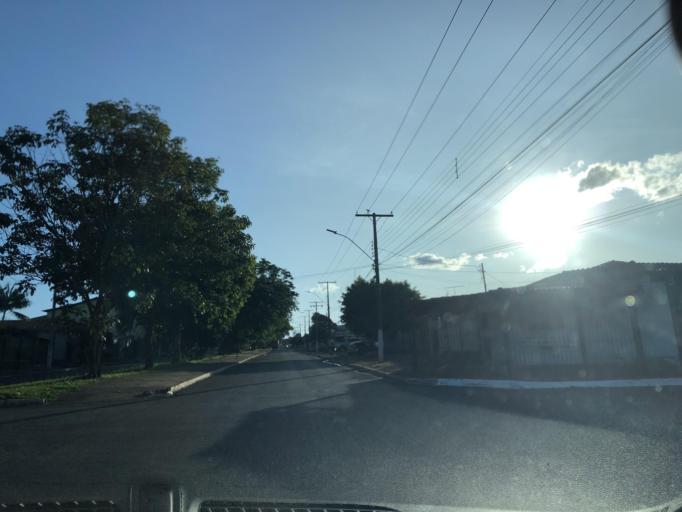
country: BR
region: Goias
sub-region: Luziania
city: Luziania
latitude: -16.2617
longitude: -47.9558
